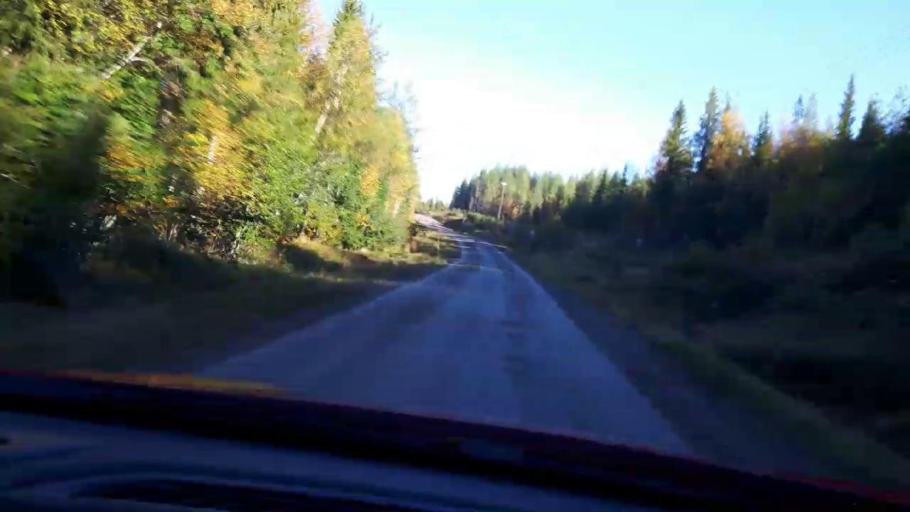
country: SE
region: Jaemtland
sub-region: Stroemsunds Kommun
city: Stroemsund
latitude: 64.3716
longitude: 15.1560
